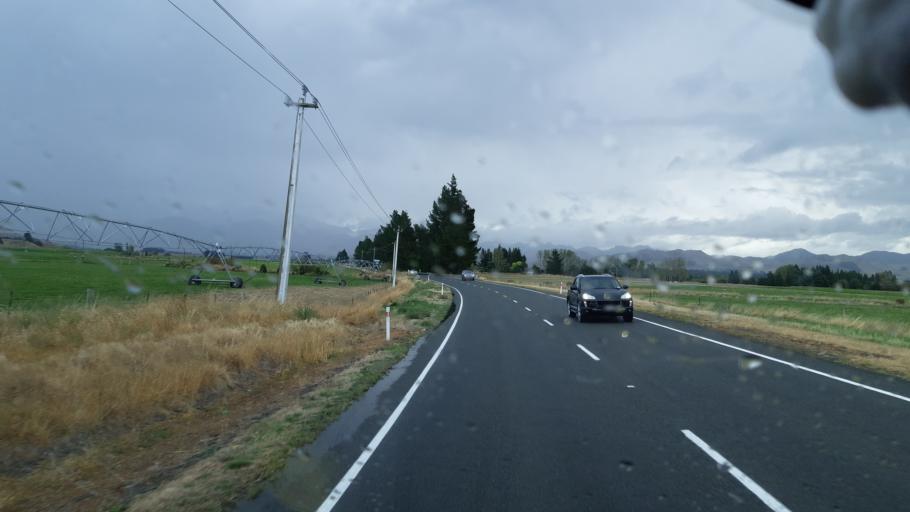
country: NZ
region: Canterbury
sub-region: Hurunui District
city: Amberley
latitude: -42.7132
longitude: 172.8614
